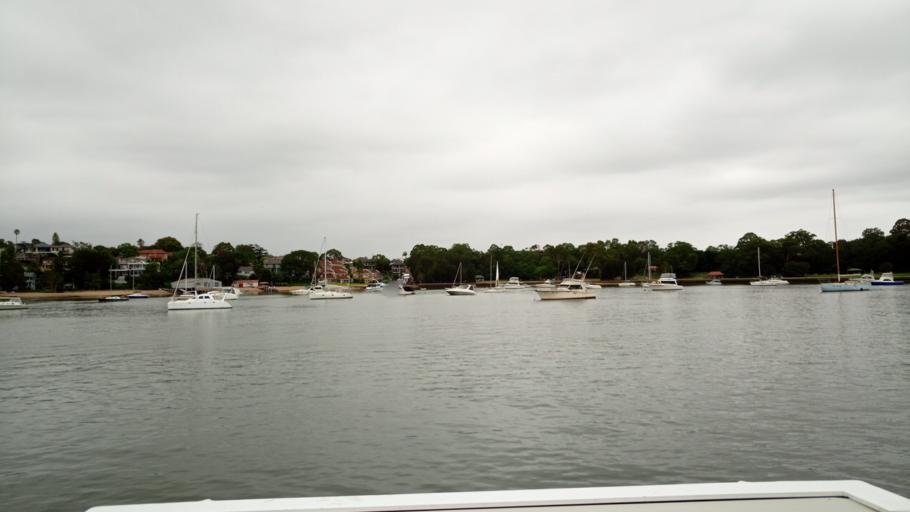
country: AU
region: New South Wales
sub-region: Canada Bay
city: Concord
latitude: -33.8336
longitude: 151.1043
